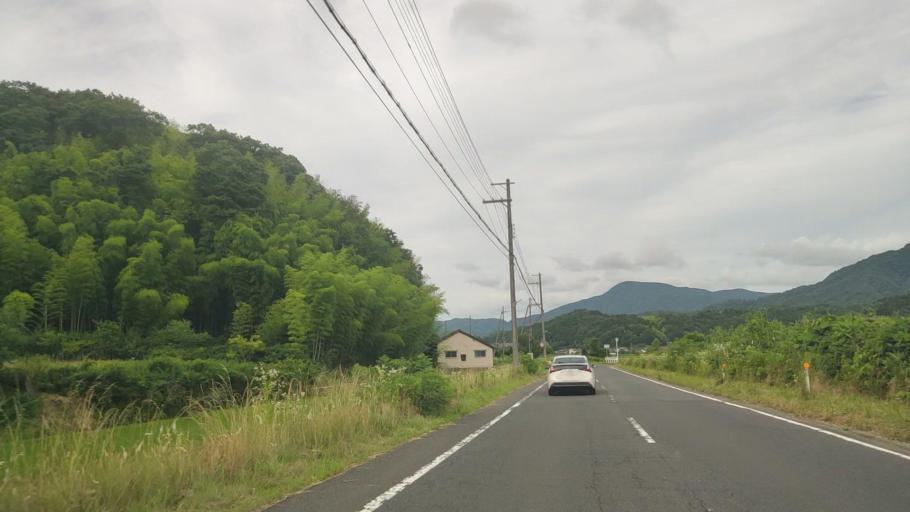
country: JP
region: Kyoto
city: Miyazu
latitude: 35.6418
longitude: 135.0811
